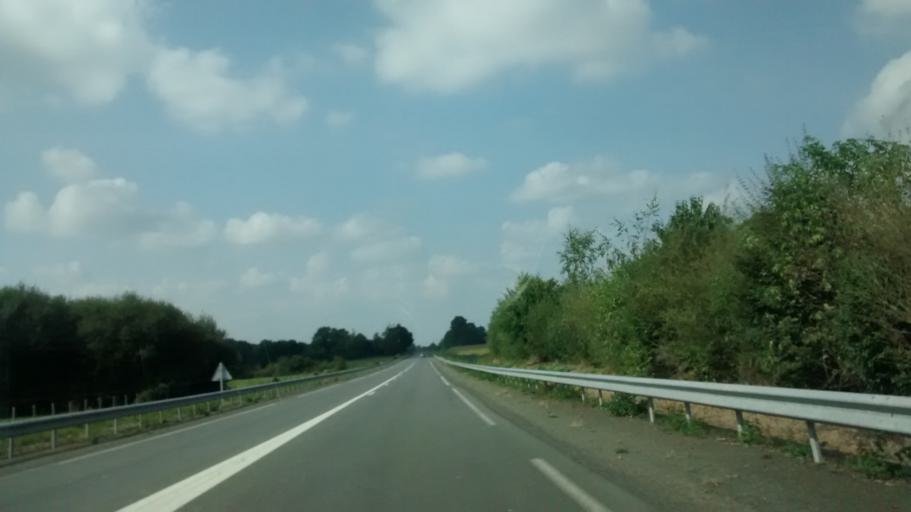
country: FR
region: Brittany
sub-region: Departement d'Ille-et-Vilaine
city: Livre-sur-Changeon
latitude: 48.2406
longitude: -1.3679
